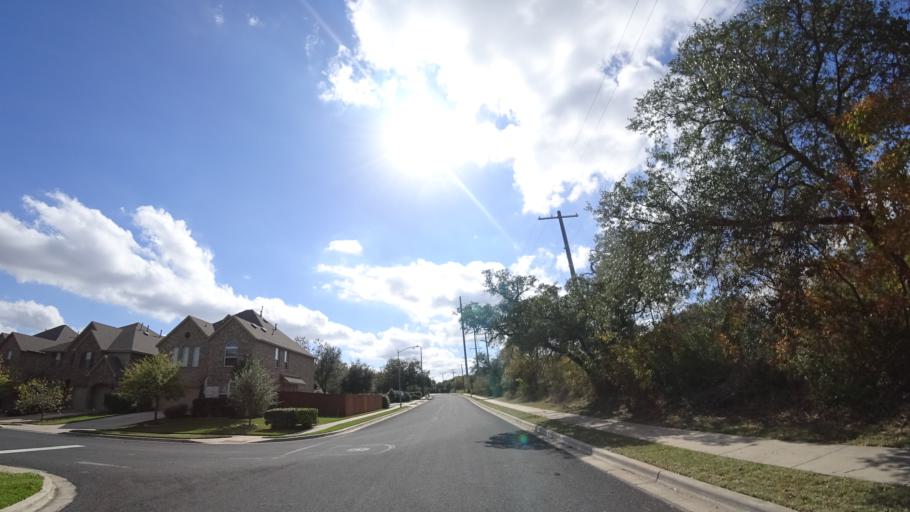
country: US
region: Texas
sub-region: Williamson County
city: Jollyville
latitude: 30.4273
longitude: -97.7297
